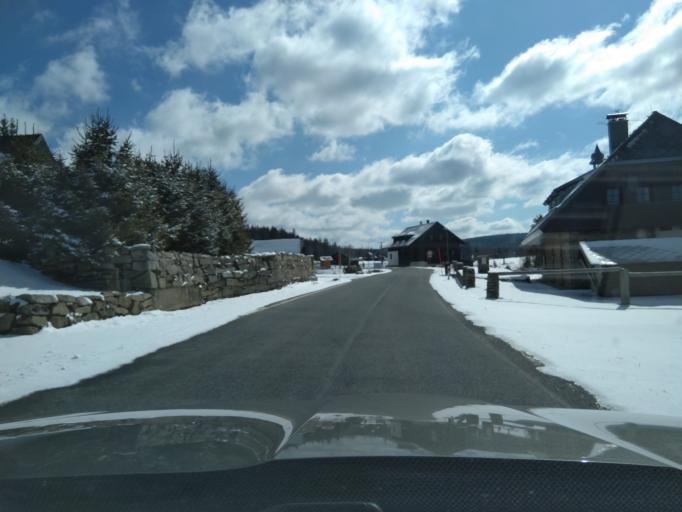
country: CZ
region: Plzensky
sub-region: Okres Klatovy
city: Kasperske Hory
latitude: 49.0520
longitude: 13.5695
